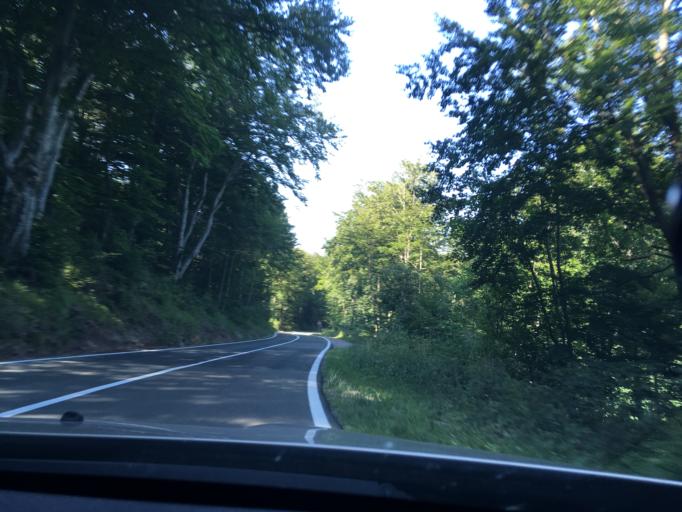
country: HR
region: Primorsko-Goranska
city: Hreljin
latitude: 45.3497
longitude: 14.6173
